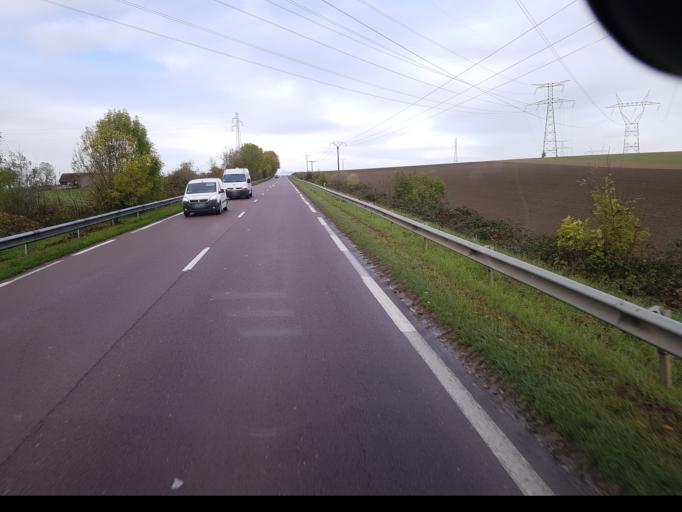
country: FR
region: Champagne-Ardenne
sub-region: Departement de l'Aube
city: Lusigny-sur-Barse
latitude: 48.2693
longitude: 4.2114
